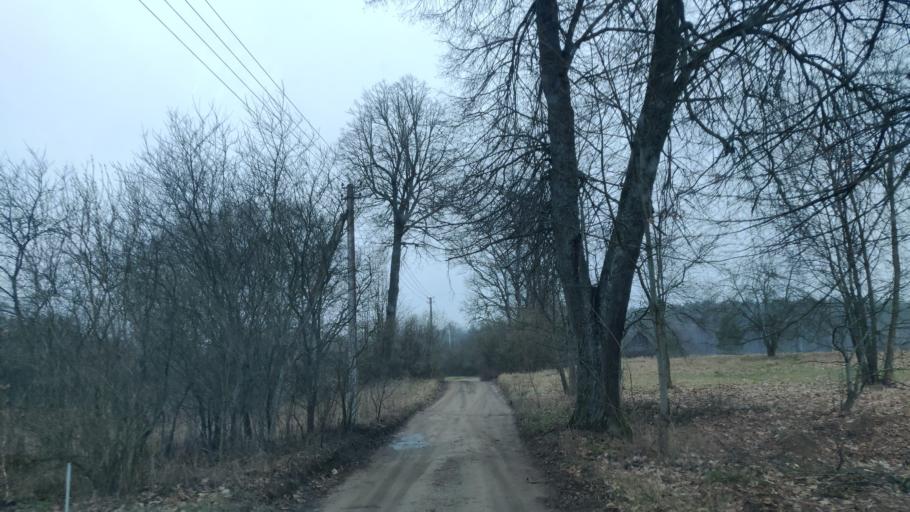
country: LT
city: Trakai
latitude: 54.5600
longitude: 24.9293
